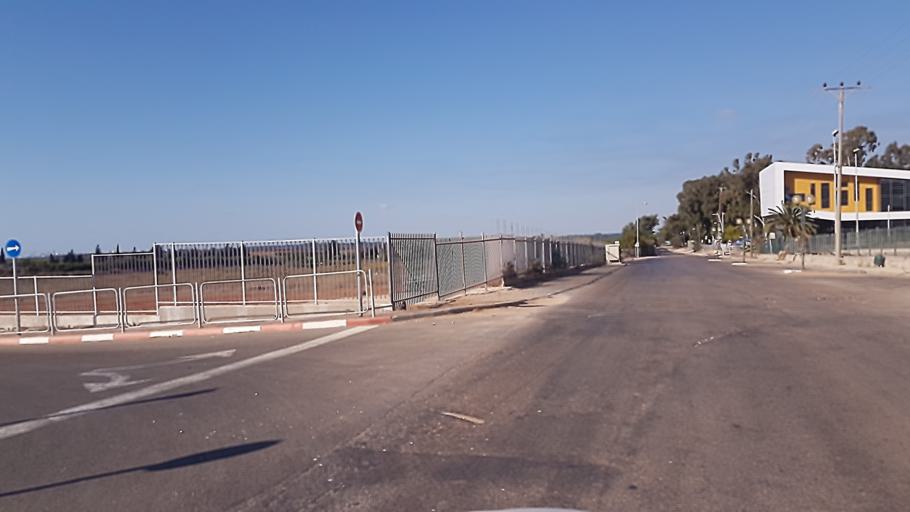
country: IL
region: Central District
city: Kfar Saba
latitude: 32.2011
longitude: 34.9237
